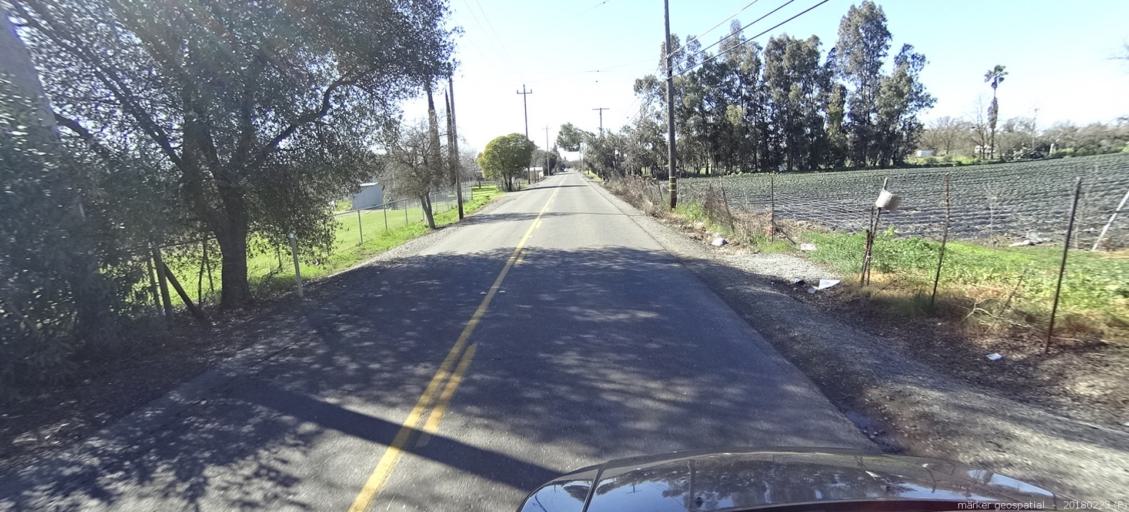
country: US
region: California
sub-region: Sacramento County
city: North Highlands
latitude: 38.7044
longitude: -121.3975
